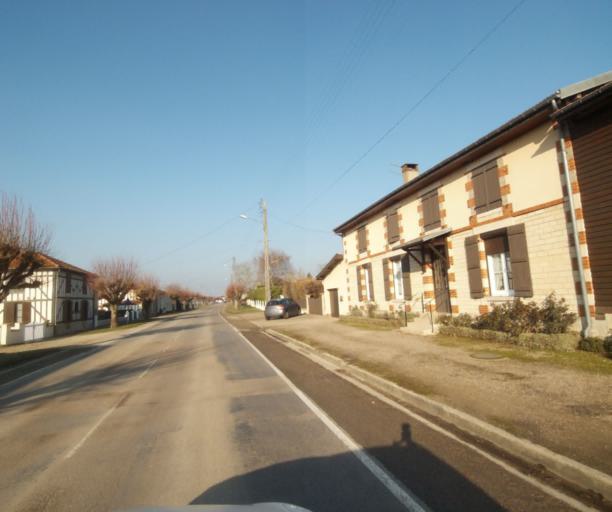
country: FR
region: Champagne-Ardenne
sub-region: Departement de la Haute-Marne
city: Montier-en-Der
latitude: 48.4822
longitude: 4.7651
